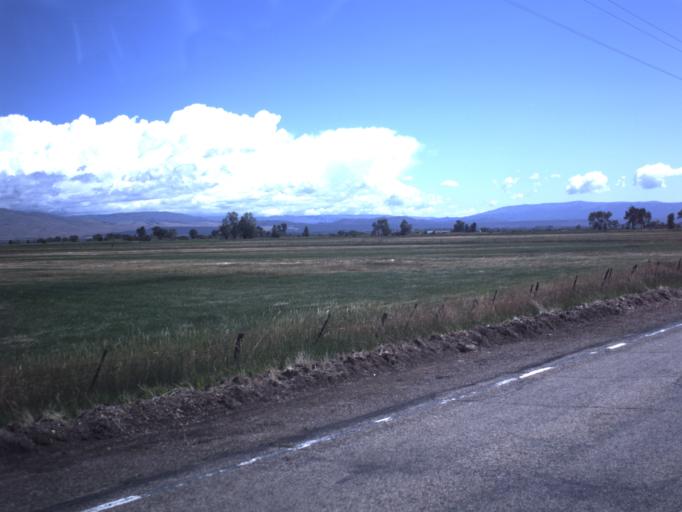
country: US
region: Utah
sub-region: Duchesne County
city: Roosevelt
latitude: 40.4329
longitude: -109.9894
